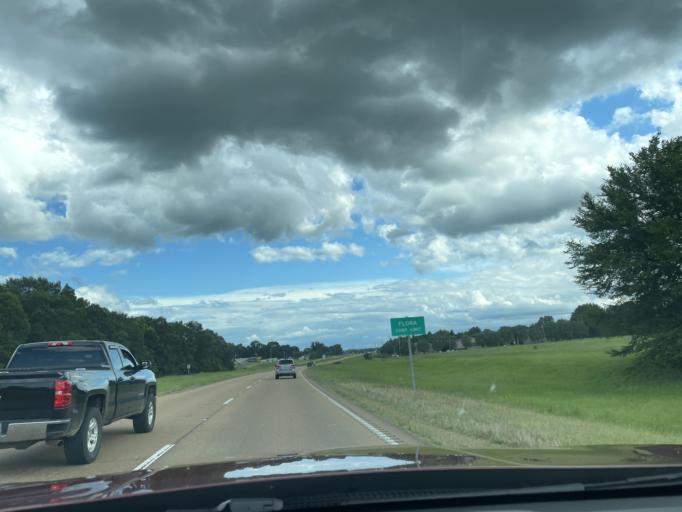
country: US
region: Mississippi
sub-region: Madison County
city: Flora
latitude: 32.5589
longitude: -90.3222
